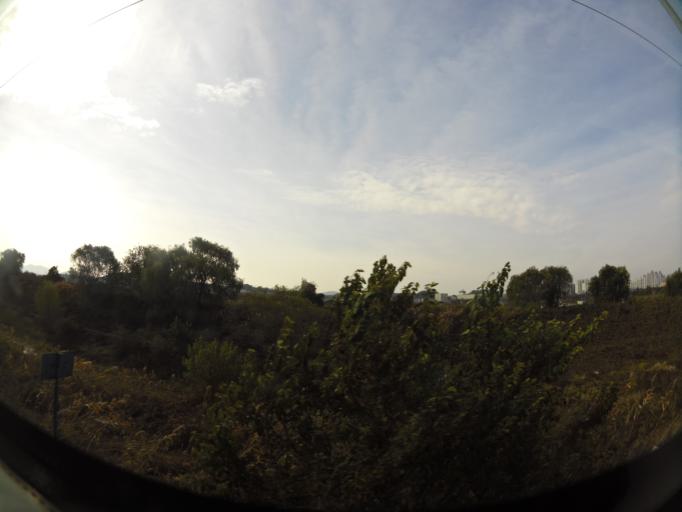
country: KR
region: Daejeon
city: Songgang-dong
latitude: 36.5861
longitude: 127.3068
